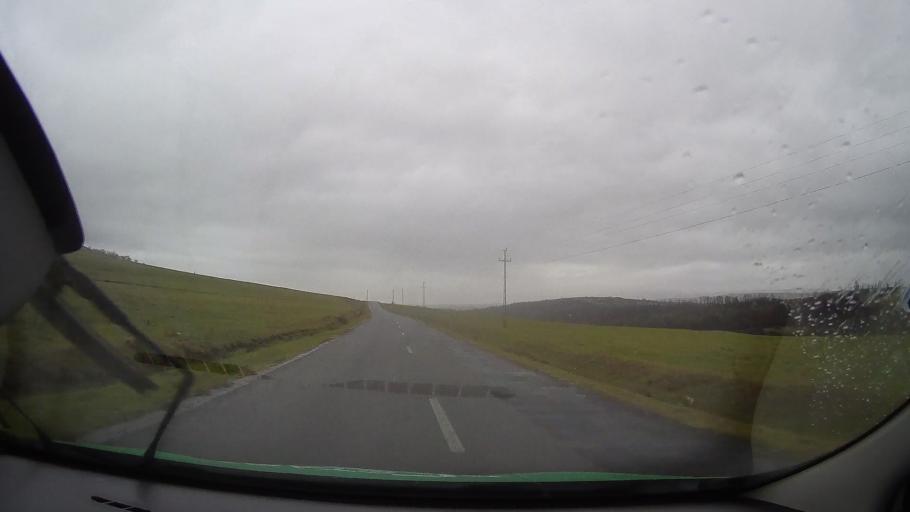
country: RO
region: Mures
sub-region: Comuna Brancovenesti
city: Valenii de Mures
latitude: 46.9125
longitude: 24.7822
